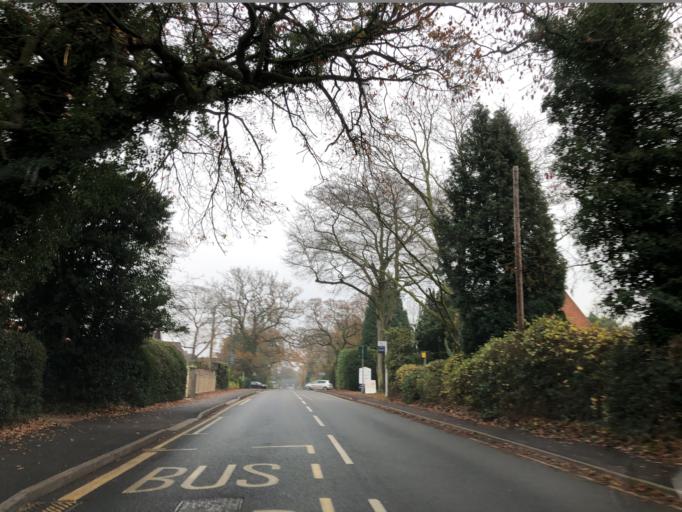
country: GB
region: England
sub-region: Solihull
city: Balsall Common
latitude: 52.3845
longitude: -1.6510
